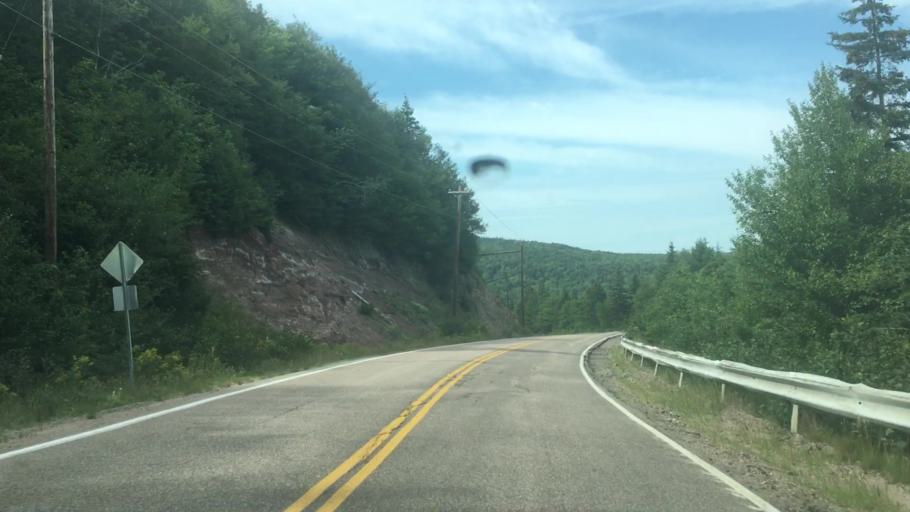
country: CA
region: Nova Scotia
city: Sydney Mines
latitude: 46.6029
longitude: -60.3853
